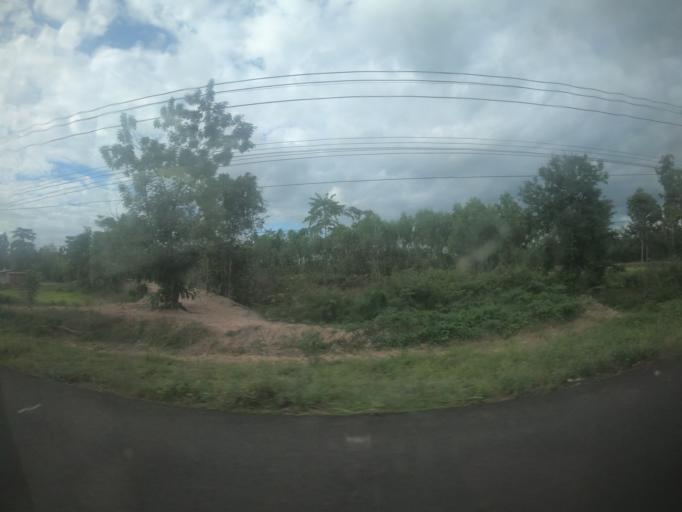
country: TH
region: Surin
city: Prasat
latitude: 14.5680
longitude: 103.4908
